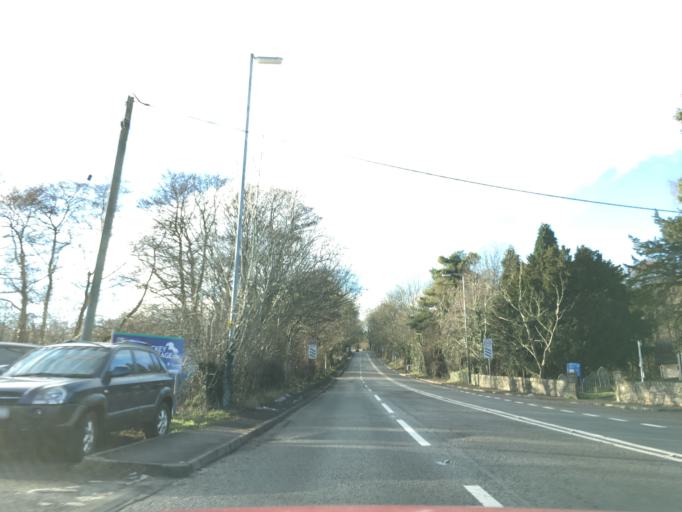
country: GB
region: Wales
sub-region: Torfaen County Borough
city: New Inn
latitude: 51.7043
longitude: -3.0111
